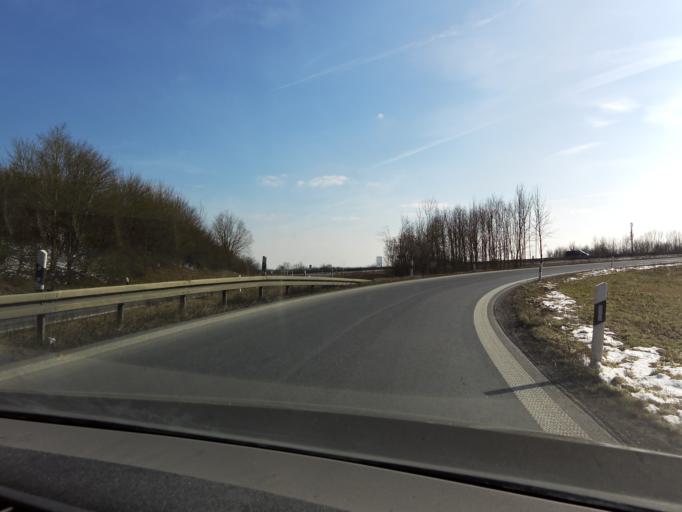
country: DE
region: Bavaria
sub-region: Regierungsbezirk Unterfranken
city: Estenfeld
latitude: 49.8475
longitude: 10.0125
